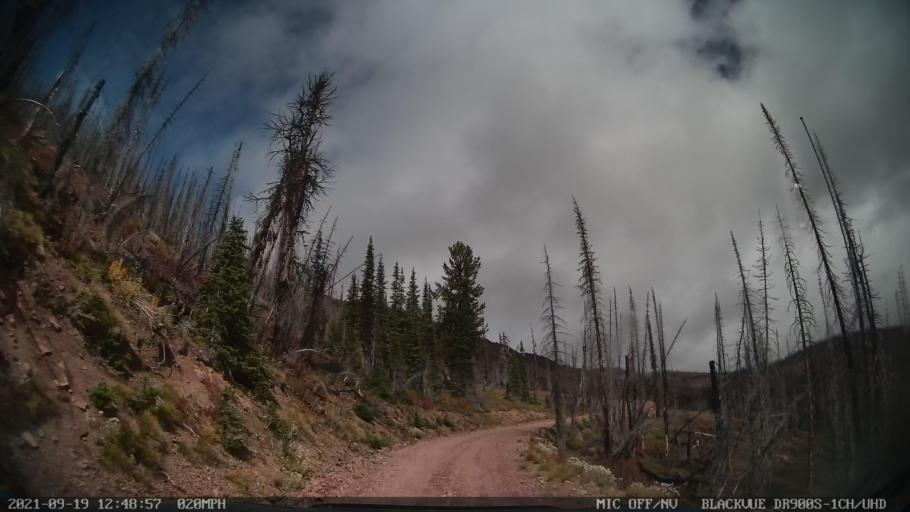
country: US
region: Montana
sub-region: Missoula County
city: Seeley Lake
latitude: 47.1880
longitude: -113.3537
